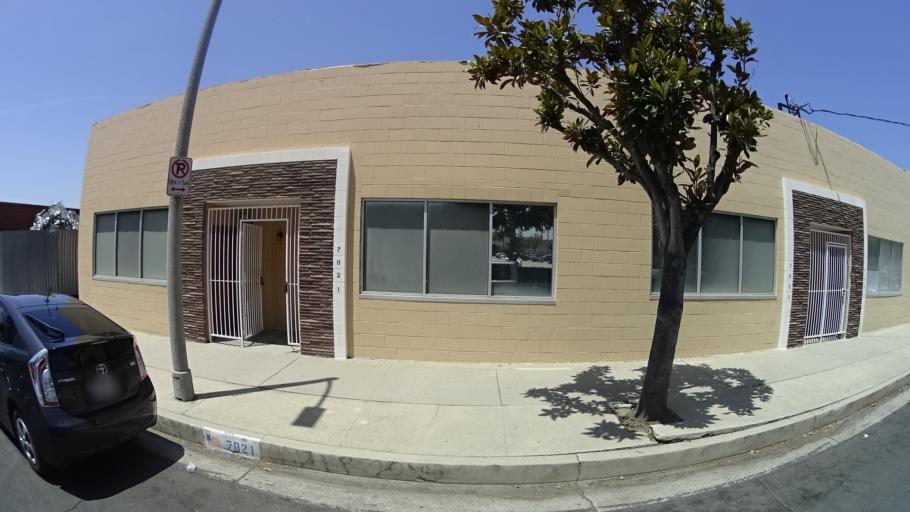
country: US
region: California
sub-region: Los Angeles County
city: Van Nuys
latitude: 34.2127
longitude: -118.4619
